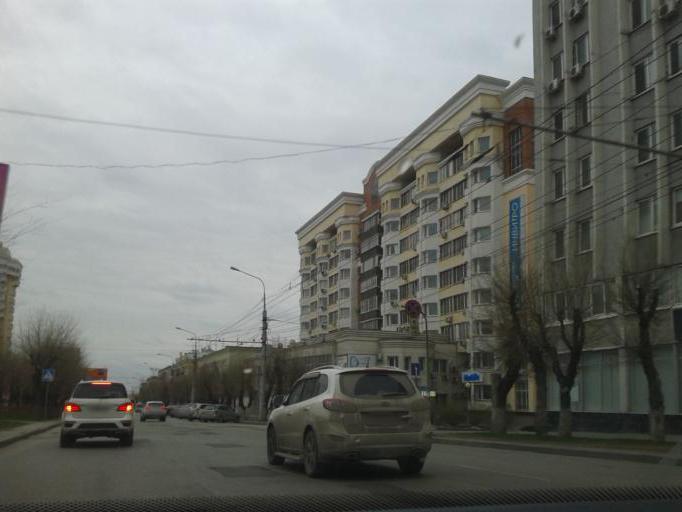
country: RU
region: Volgograd
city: Volgograd
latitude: 48.7183
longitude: 44.5076
